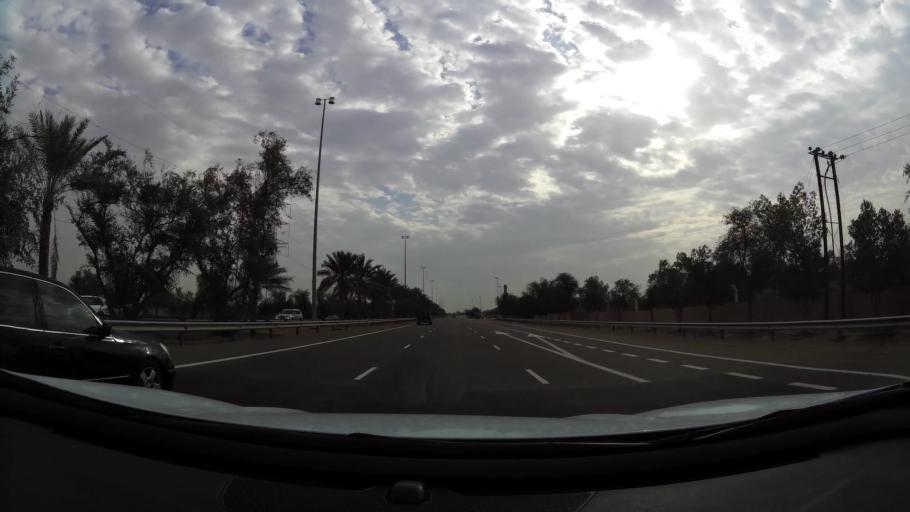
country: AE
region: Abu Dhabi
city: Al Ain
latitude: 24.2039
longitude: 55.4137
